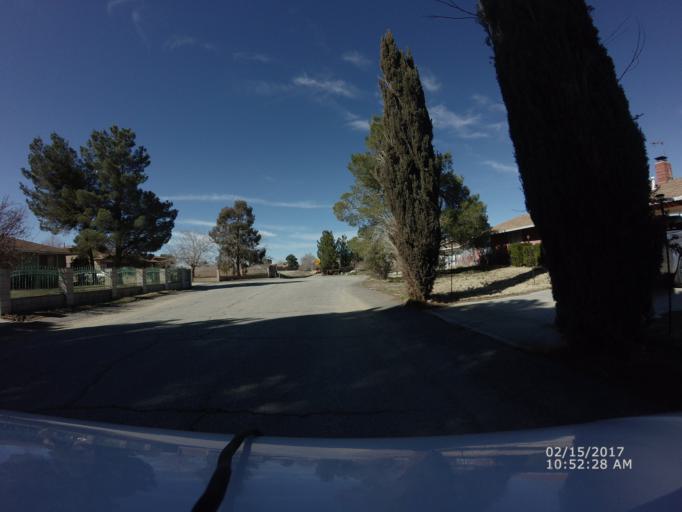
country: US
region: California
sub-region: Los Angeles County
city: Lake Los Angeles
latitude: 34.5836
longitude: -117.8497
